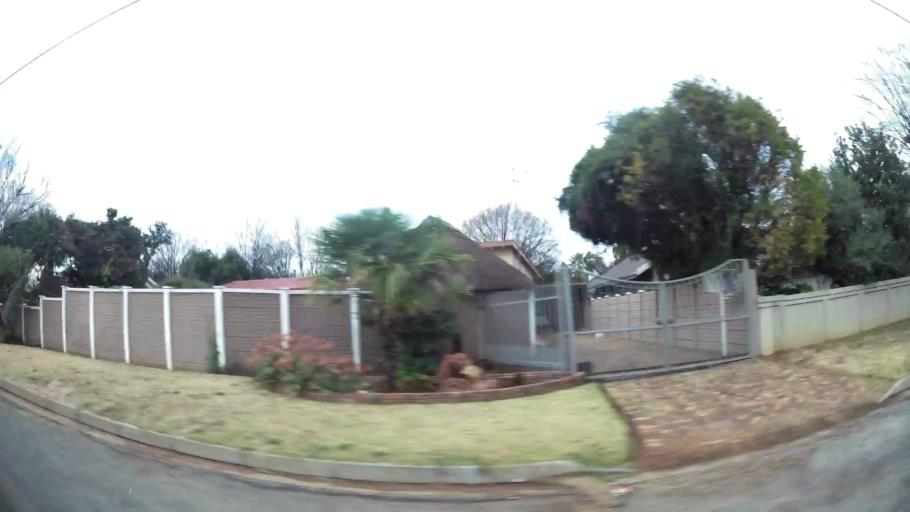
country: ZA
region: Gauteng
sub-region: Sedibeng District Municipality
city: Vereeniging
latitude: -26.6421
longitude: 27.9784
